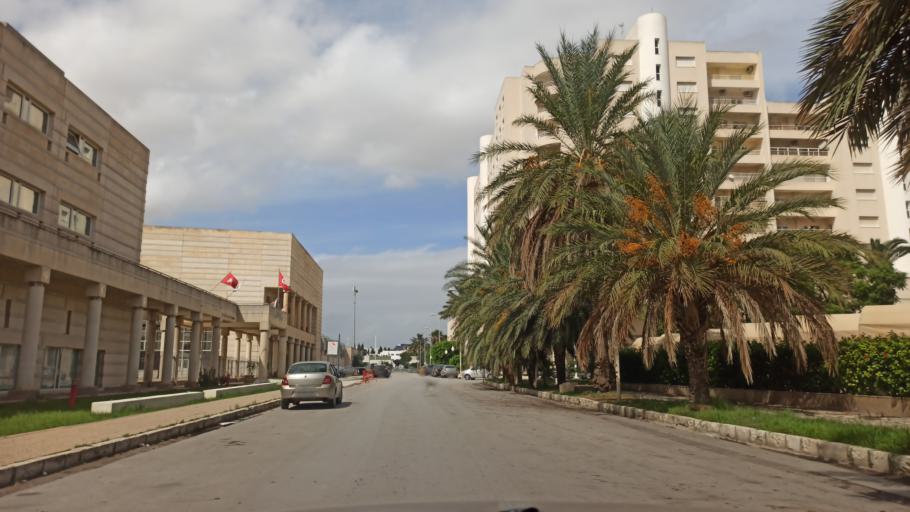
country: TN
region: Ariana
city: Ariana
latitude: 36.8478
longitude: 10.1903
